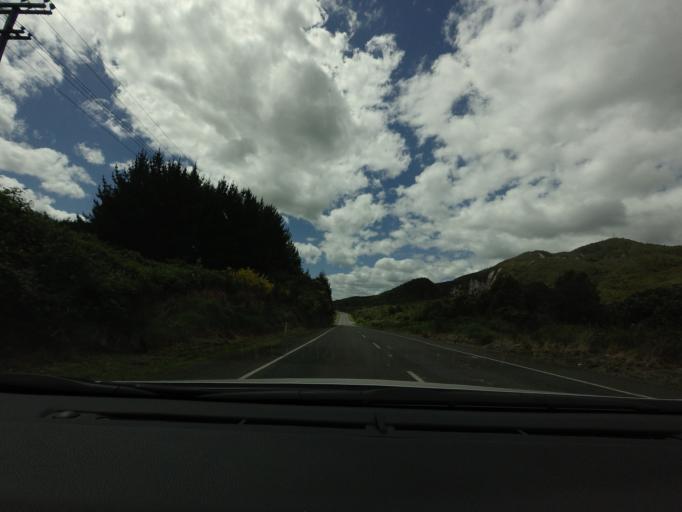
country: NZ
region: Bay of Plenty
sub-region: Rotorua District
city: Rotorua
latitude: -38.3233
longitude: 176.3715
